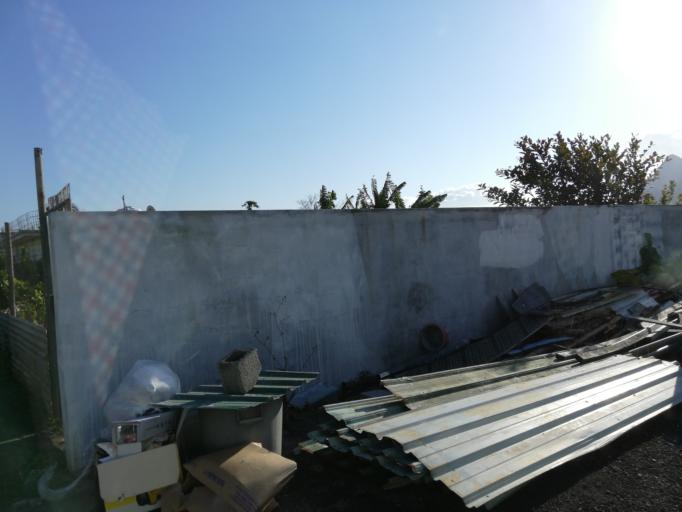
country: MU
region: Moka
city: Saint Pierre
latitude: -20.2185
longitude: 57.5239
